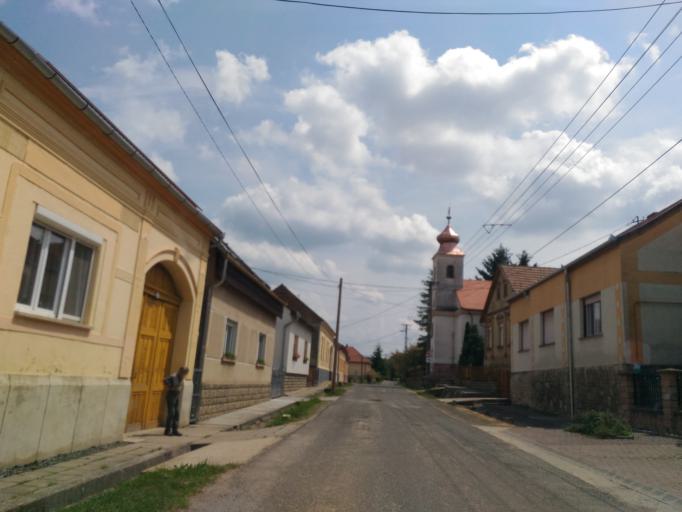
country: HU
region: Baranya
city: Komlo
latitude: 46.1957
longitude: 18.2274
